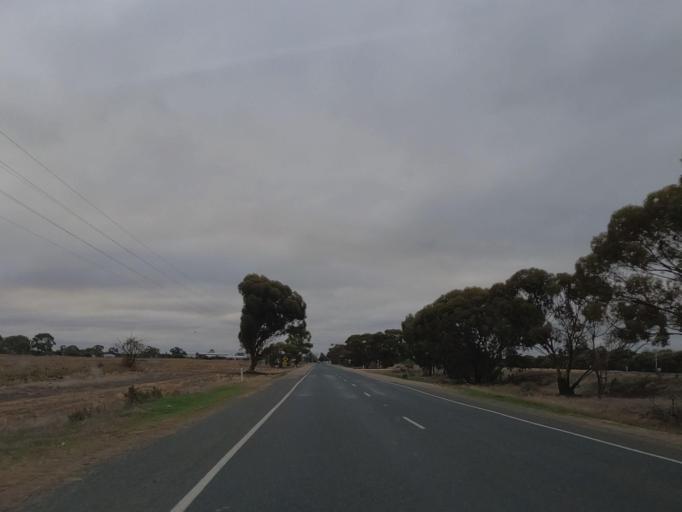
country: AU
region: Victoria
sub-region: Swan Hill
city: Swan Hill
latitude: -35.3940
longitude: 143.5719
